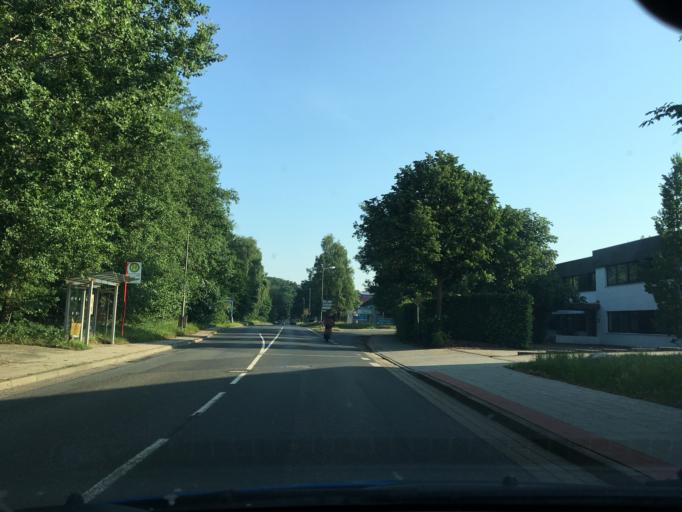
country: DE
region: Lower Saxony
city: Buchholz in der Nordheide
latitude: 53.3449
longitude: 9.8575
